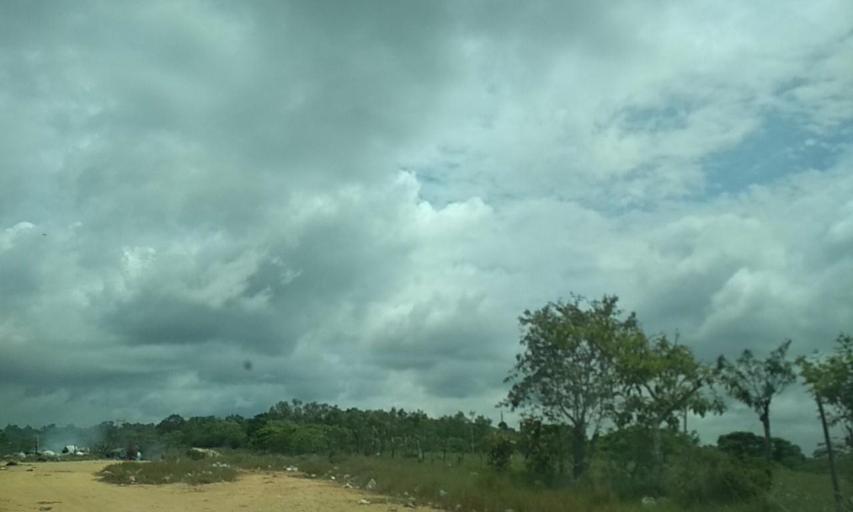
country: MX
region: Veracruz
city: Las Choapas
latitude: 17.9081
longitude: -94.1256
